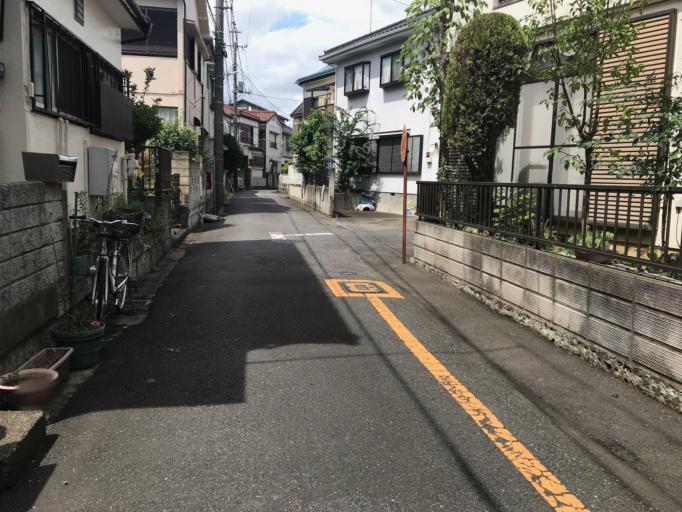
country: JP
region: Tokyo
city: Tanashicho
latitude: 35.7669
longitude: 139.5526
